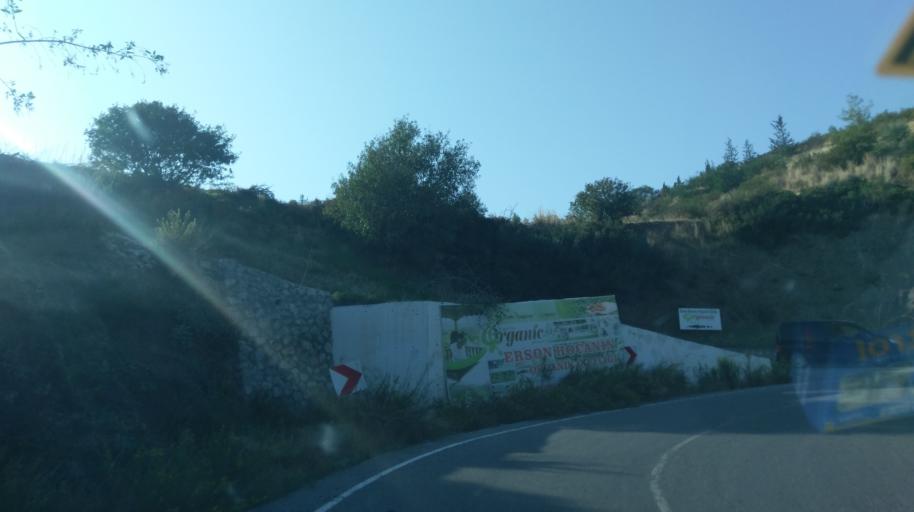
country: CY
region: Lefkosia
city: Kato Pyrgos
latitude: 35.1692
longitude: 32.7268
